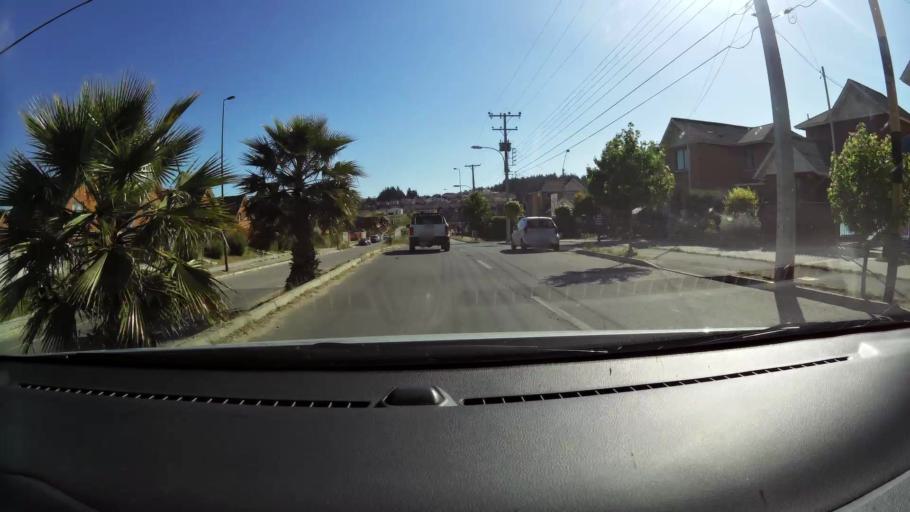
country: CL
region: Valparaiso
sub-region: Provincia de Valparaiso
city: Vina del Mar
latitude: -33.1273
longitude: -71.5663
